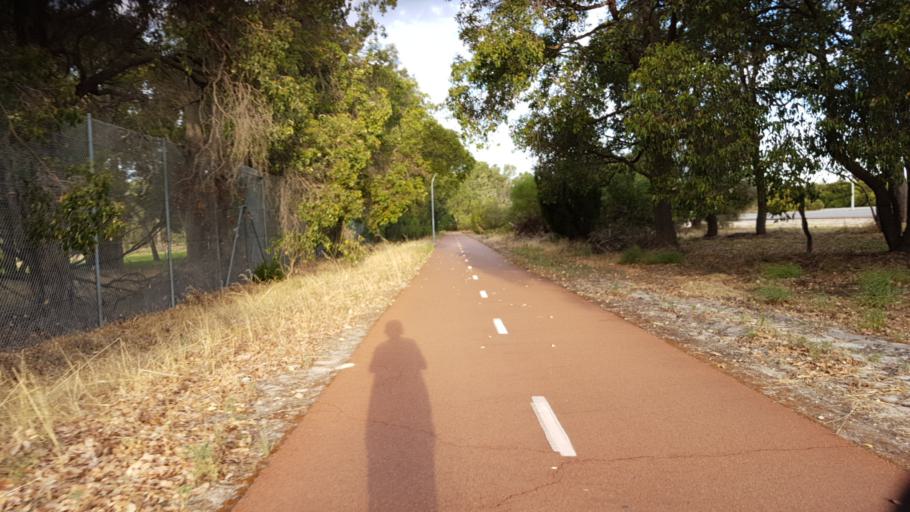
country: AU
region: Western Australia
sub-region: Canning
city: Canning Vale
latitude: -32.0544
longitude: 115.9238
